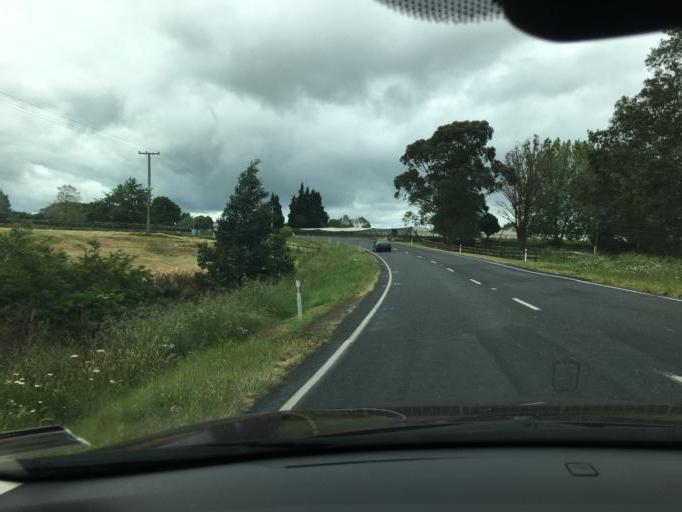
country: NZ
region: Waikato
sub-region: Waipa District
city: Cambridge
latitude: -37.9151
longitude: 175.4485
